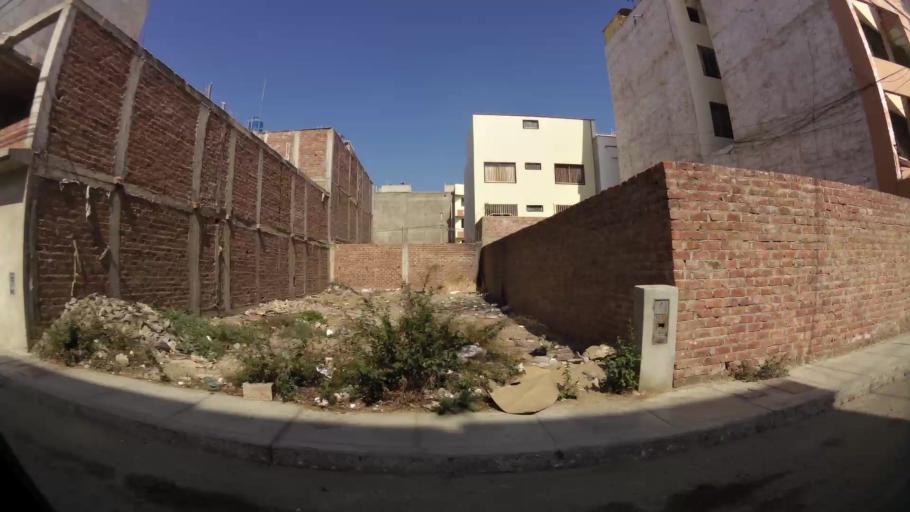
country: PE
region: La Libertad
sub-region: Provincia de Trujillo
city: Trujillo
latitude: -8.1291
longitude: -79.0308
